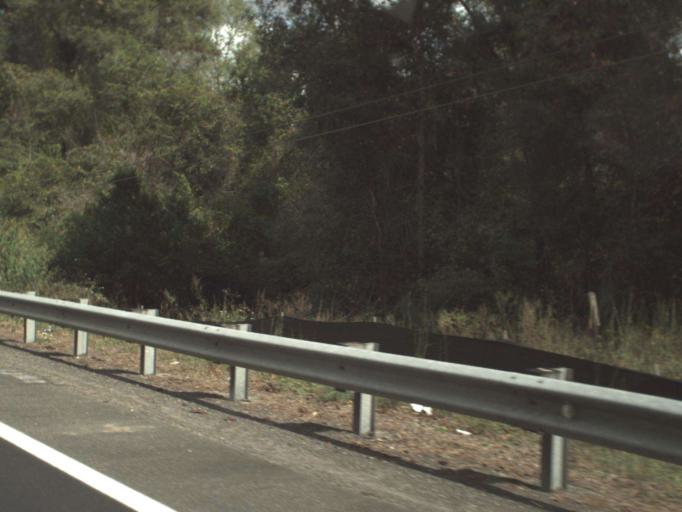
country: US
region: Florida
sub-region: Gadsden County
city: Havana
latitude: 30.5904
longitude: -84.4847
